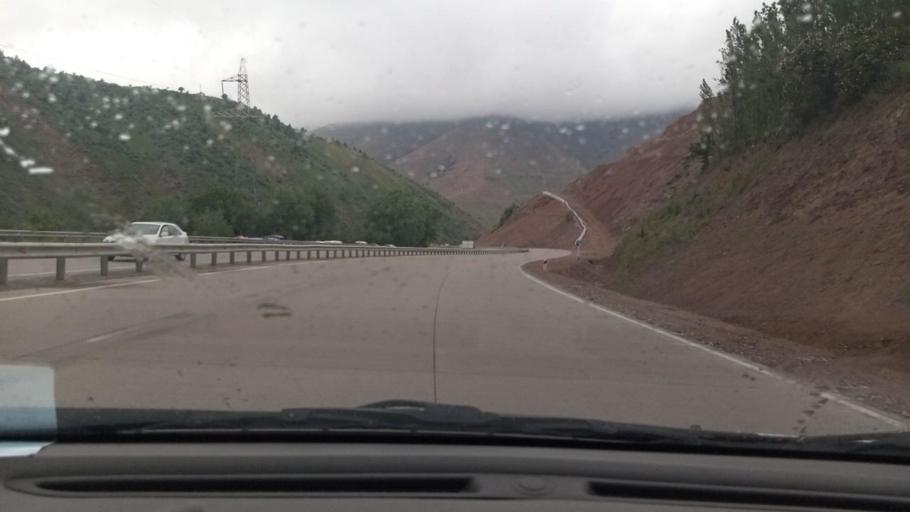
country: UZ
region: Toshkent
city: Angren
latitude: 41.1424
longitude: 70.4500
